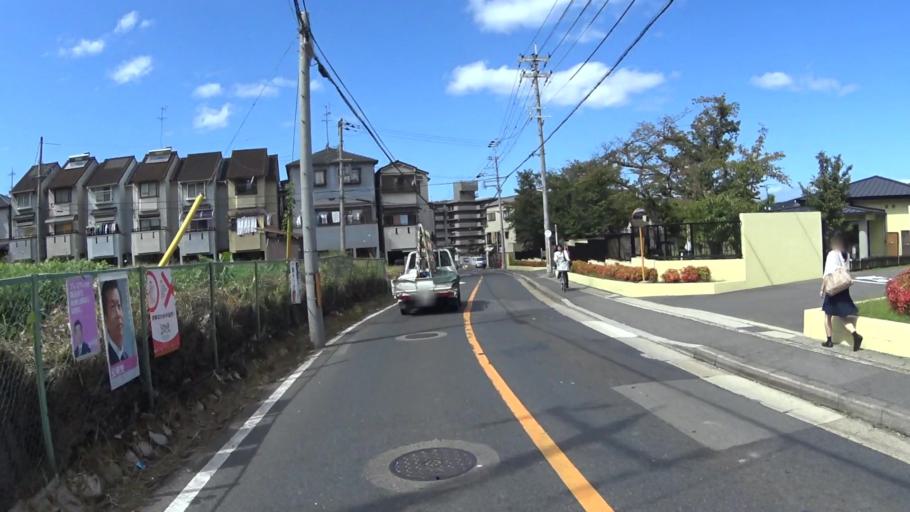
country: JP
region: Kyoto
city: Uji
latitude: 34.9370
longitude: 135.8101
